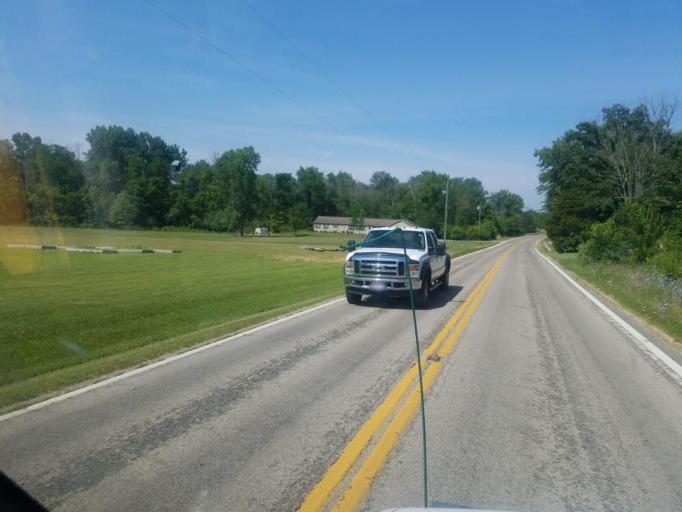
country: US
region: Ohio
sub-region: Union County
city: Marysville
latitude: 40.2241
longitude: -83.4593
